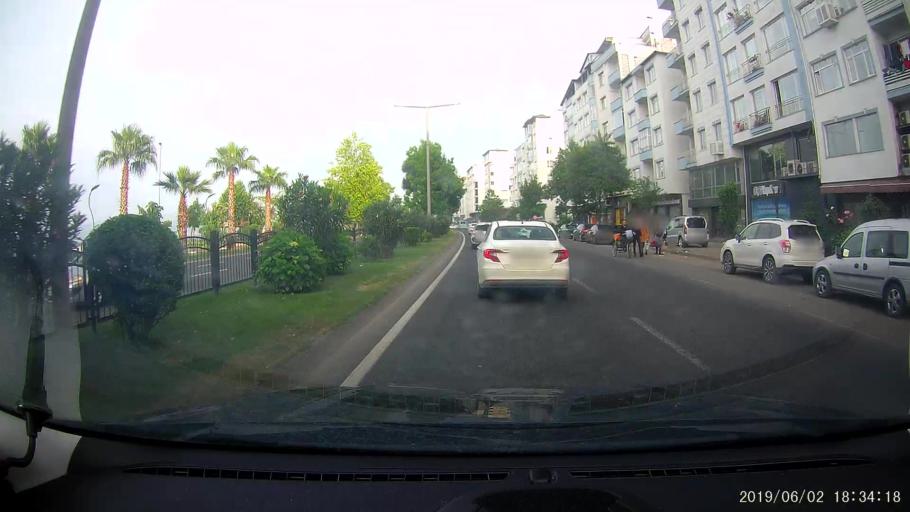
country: TR
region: Ordu
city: Fatsa
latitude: 41.0301
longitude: 37.5028
